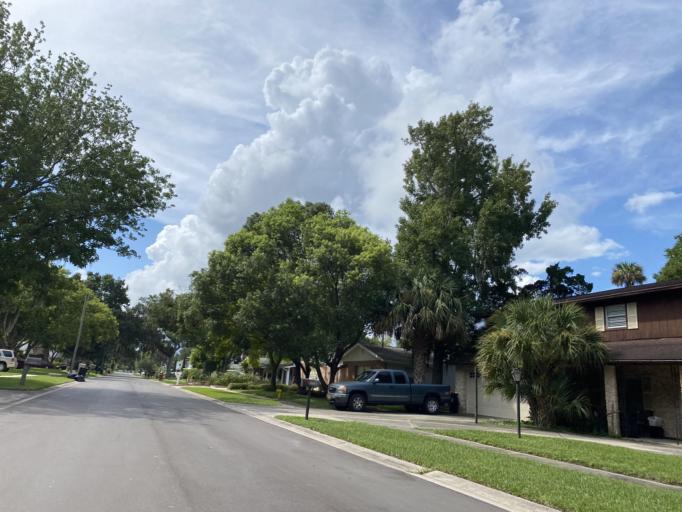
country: US
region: Florida
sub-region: Volusia County
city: Port Orange
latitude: 29.1359
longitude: -81.0055
